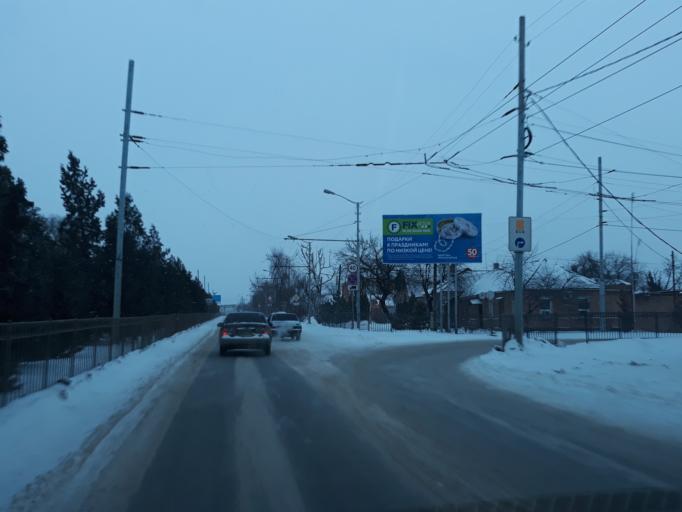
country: RU
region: Rostov
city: Taganrog
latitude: 47.2691
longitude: 38.9222
